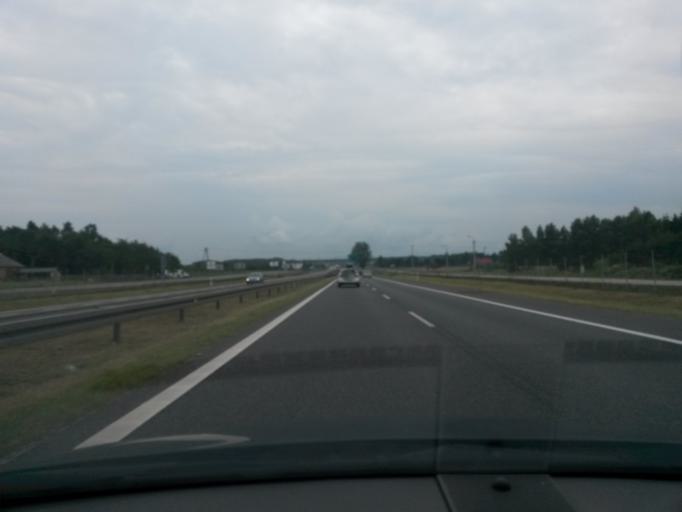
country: PL
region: Masovian Voivodeship
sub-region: Powiat zyrardowski
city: Mszczonow
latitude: 51.9479
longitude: 20.4877
